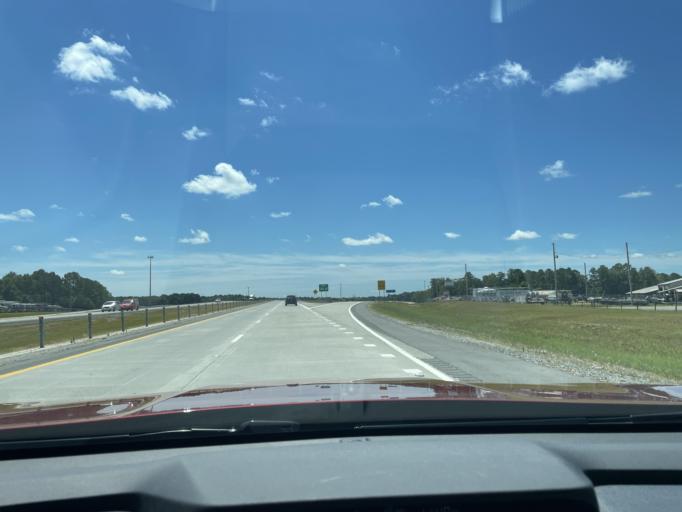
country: US
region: Arkansas
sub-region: Jefferson County
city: White Hall
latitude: 34.2310
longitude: -92.0811
